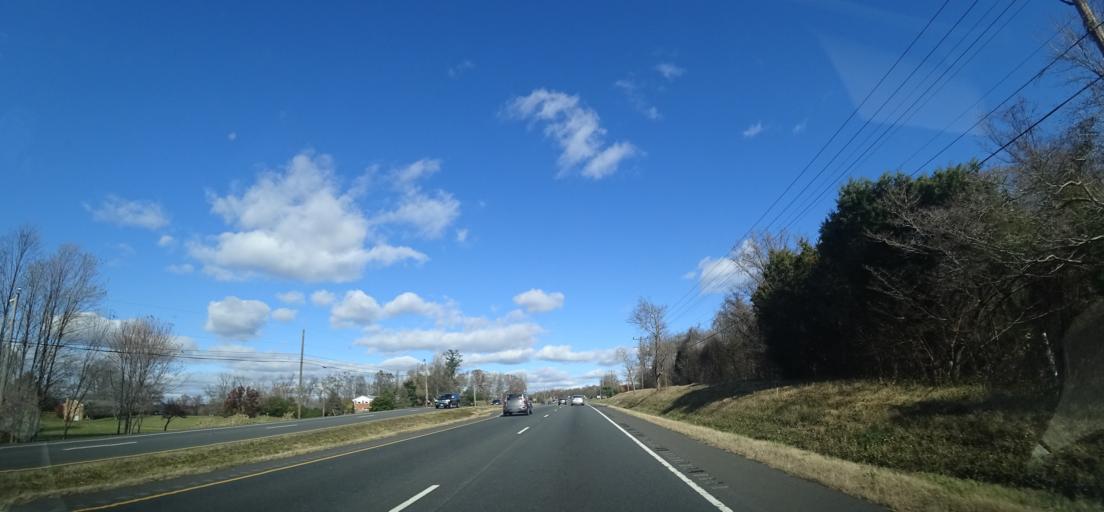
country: US
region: Virginia
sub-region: Fauquier County
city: Warrenton
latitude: 38.6673
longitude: -77.7948
